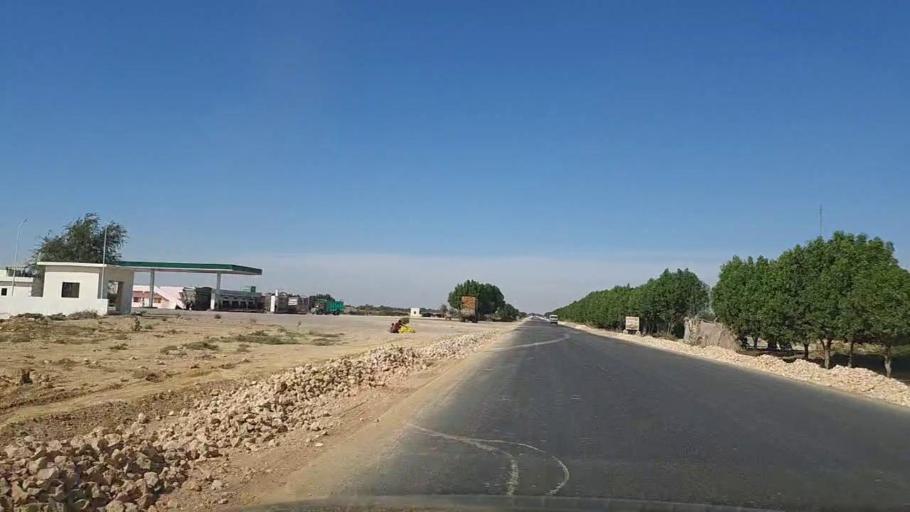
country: PK
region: Sindh
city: Kotri
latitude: 25.2675
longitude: 68.2189
